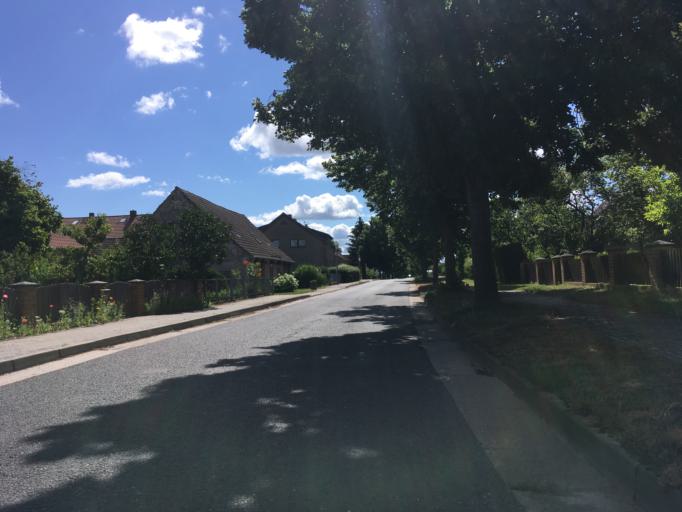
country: DE
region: Brandenburg
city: Templin
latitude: 53.1726
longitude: 13.5569
